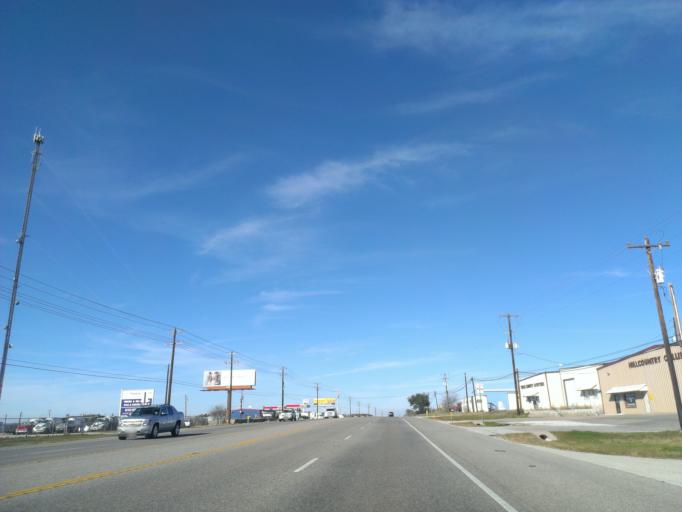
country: US
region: Texas
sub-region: Burnet County
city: Meadowlakes
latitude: 30.5447
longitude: -98.2771
